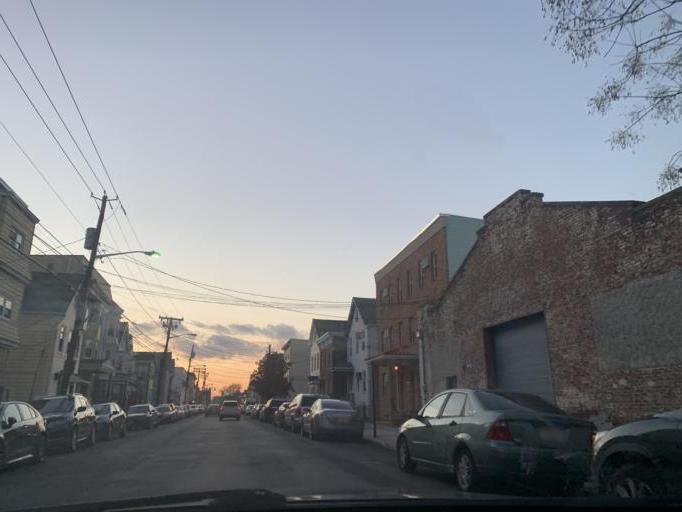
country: US
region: New Jersey
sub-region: Hudson County
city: Harrison
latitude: 40.7482
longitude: -74.1546
